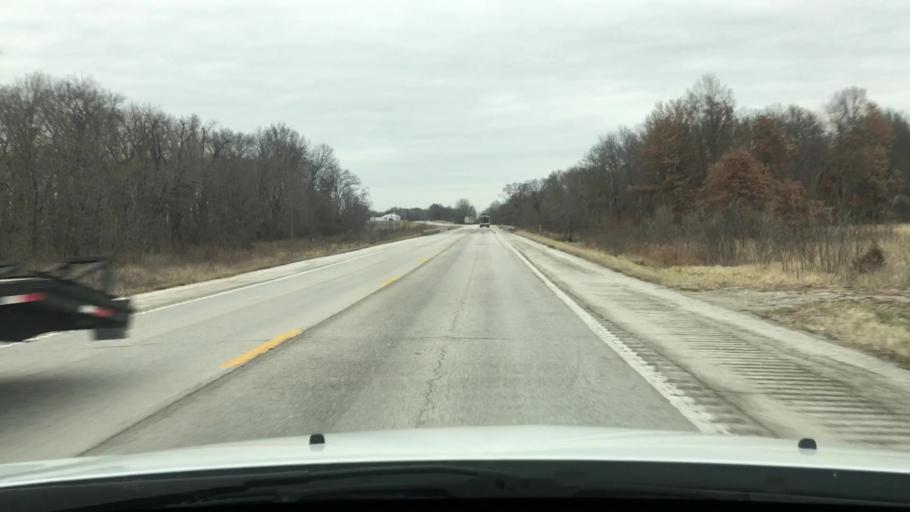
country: US
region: Missouri
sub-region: Montgomery County
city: Wellsville
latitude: 39.1986
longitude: -91.6465
